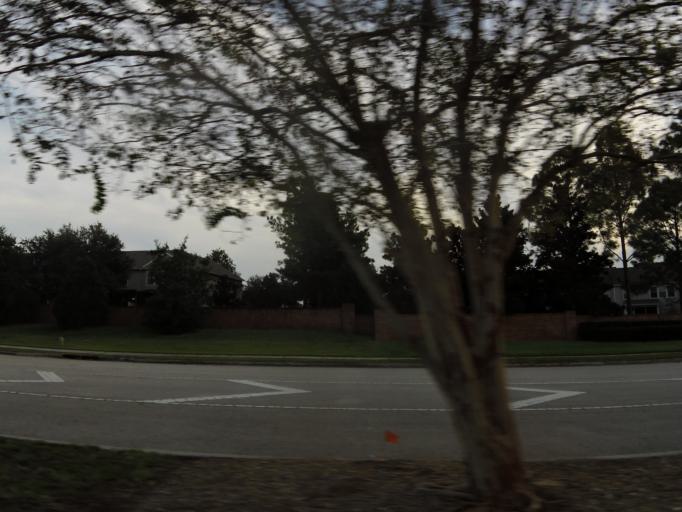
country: US
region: Florida
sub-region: Saint Johns County
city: Ponte Vedra Beach
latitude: 30.2480
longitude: -81.5236
